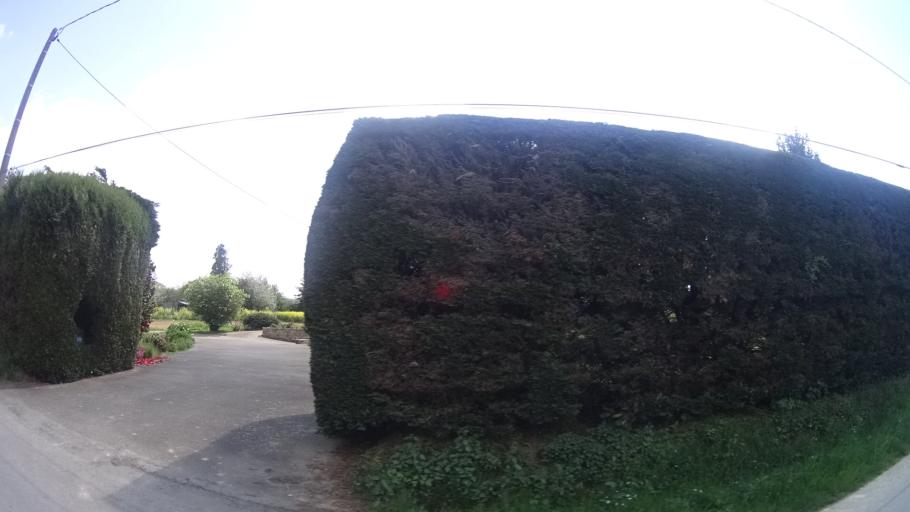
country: FR
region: Brittany
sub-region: Departement du Morbihan
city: Allaire
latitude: 47.6006
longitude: -2.1796
